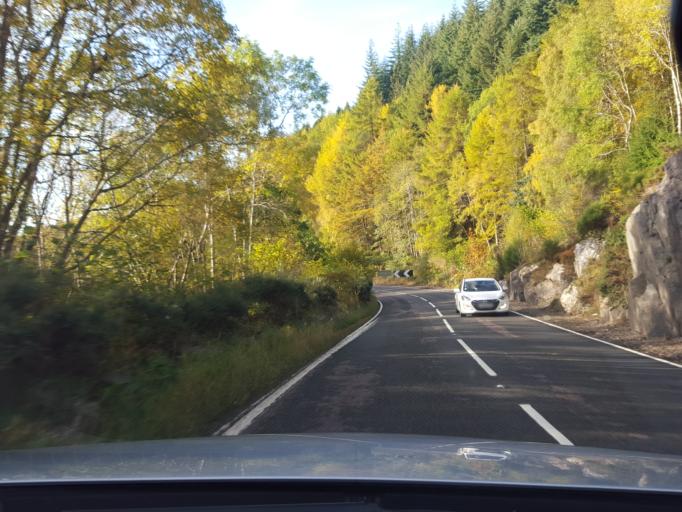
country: GB
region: Scotland
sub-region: Highland
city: Beauly
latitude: 57.3434
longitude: -4.4226
